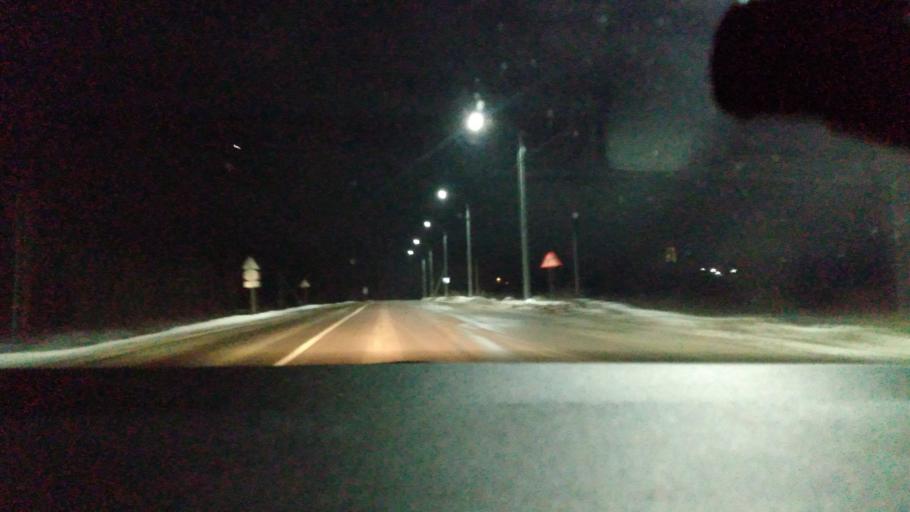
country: RU
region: Moskovskaya
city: Krasnaya Poyma
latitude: 55.1675
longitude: 39.1576
